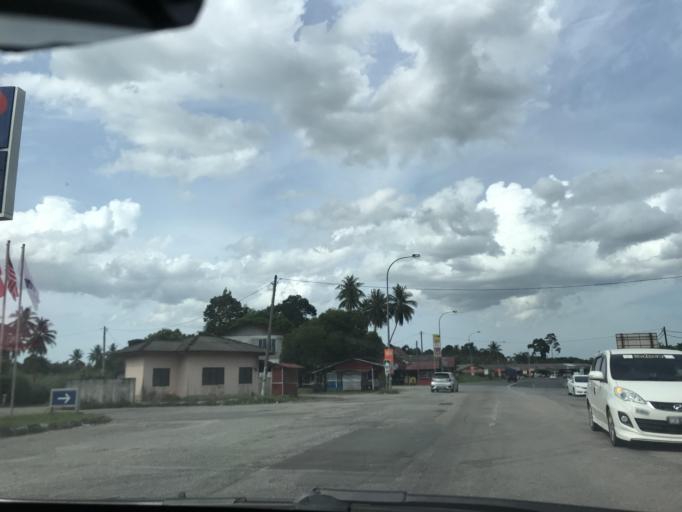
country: MY
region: Kelantan
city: Kampung Lemal
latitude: 6.0340
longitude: 102.1508
